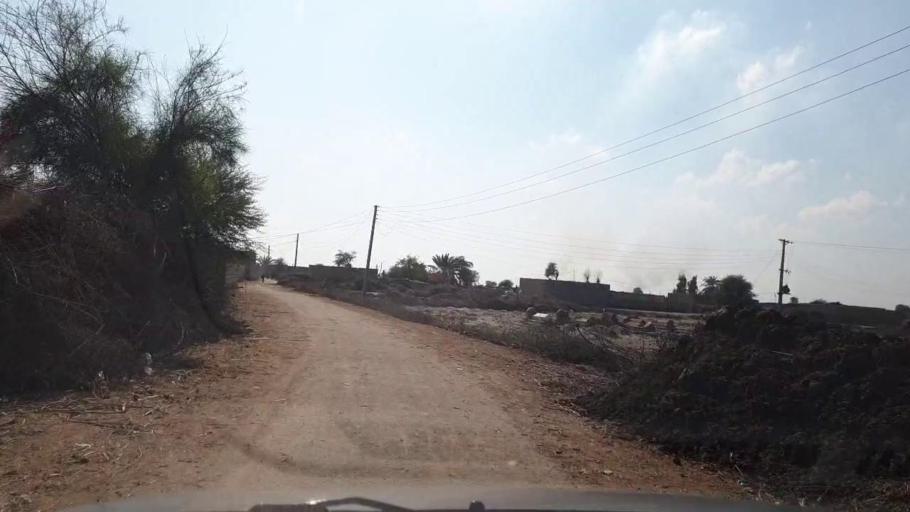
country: PK
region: Sindh
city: Khadro
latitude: 26.0794
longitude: 68.7446
